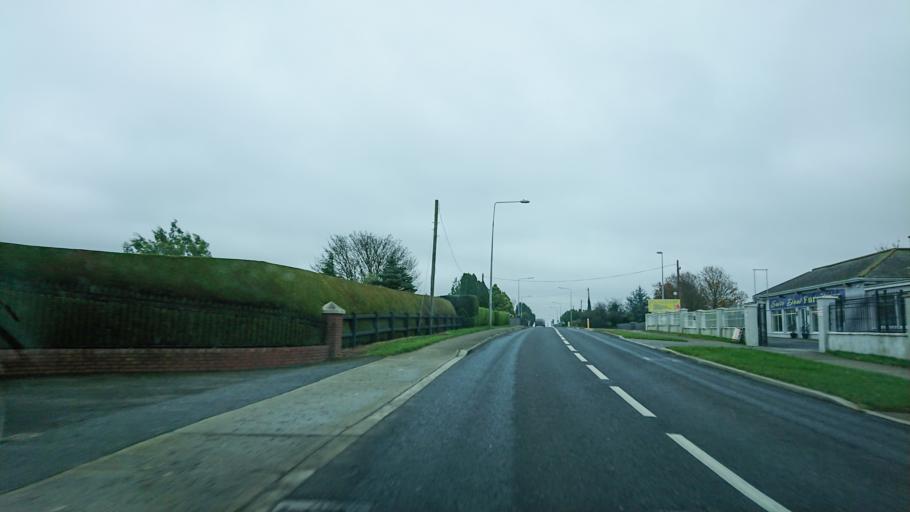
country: IE
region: Leinster
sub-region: Kilkenny
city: Mooncoin
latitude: 52.2911
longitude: -7.2482
